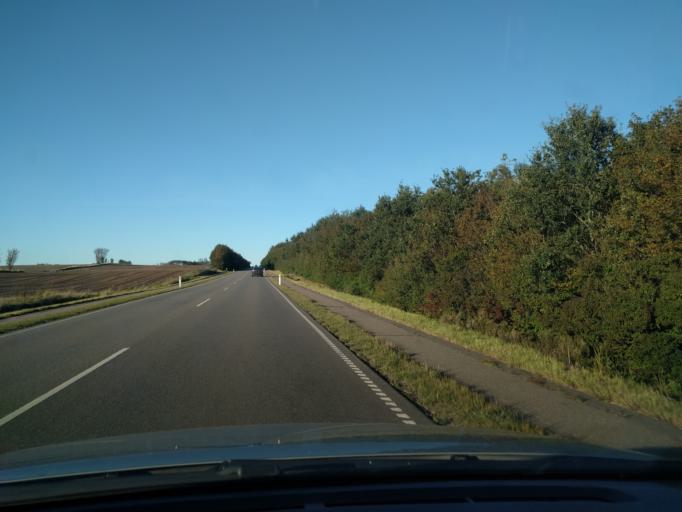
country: DK
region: Central Jutland
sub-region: Skanderborg Kommune
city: Ry
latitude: 56.1257
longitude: 9.7919
